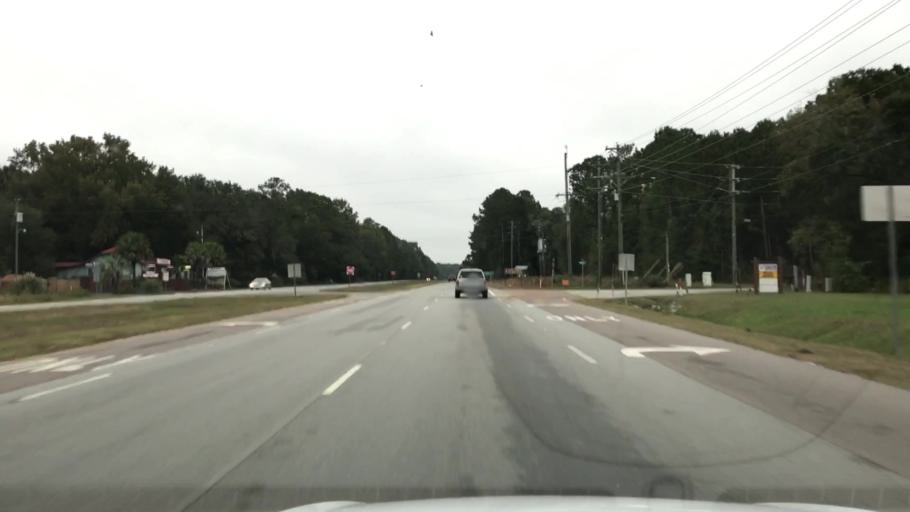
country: US
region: South Carolina
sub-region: Charleston County
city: Awendaw
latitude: 32.9256
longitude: -79.7145
